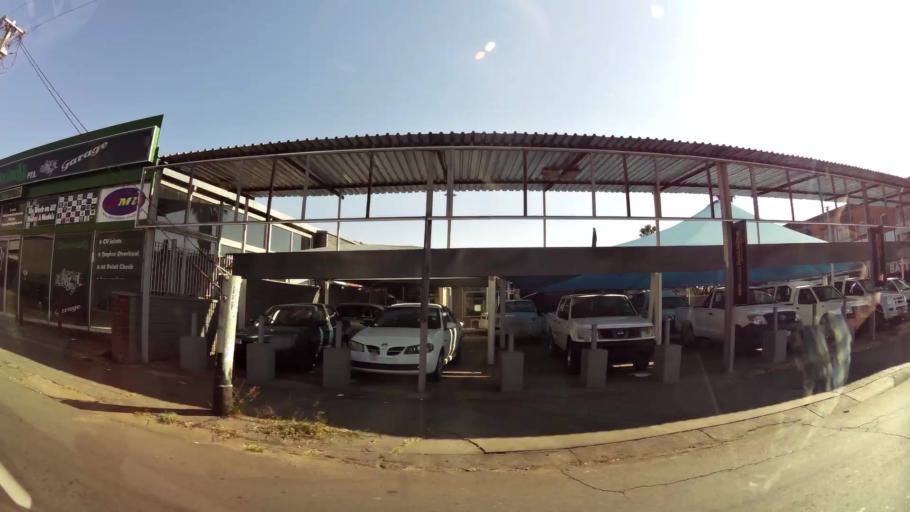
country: ZA
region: Gauteng
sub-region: City of Tshwane Metropolitan Municipality
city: Pretoria
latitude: -25.7241
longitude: 28.2034
